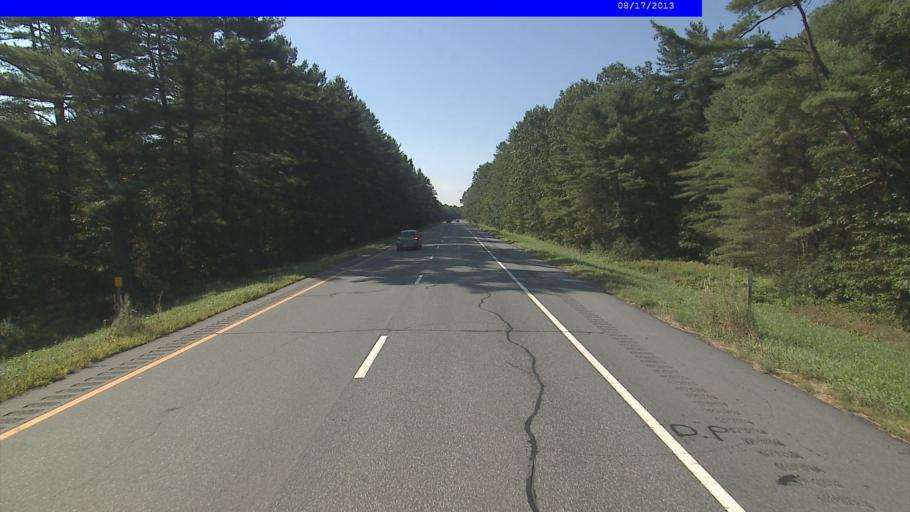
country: US
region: Vermont
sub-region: Windsor County
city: Windsor
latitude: 43.5559
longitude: -72.3855
